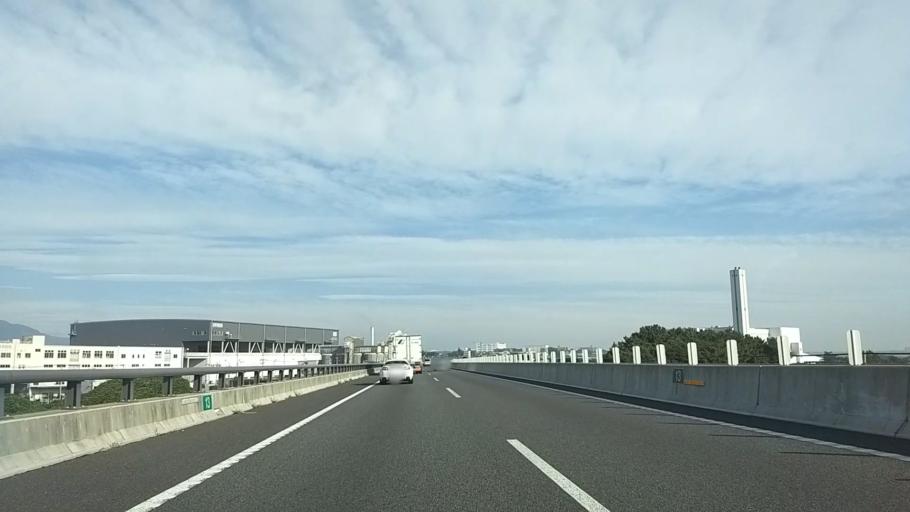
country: JP
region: Kanagawa
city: Atsugi
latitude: 35.4540
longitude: 139.3738
